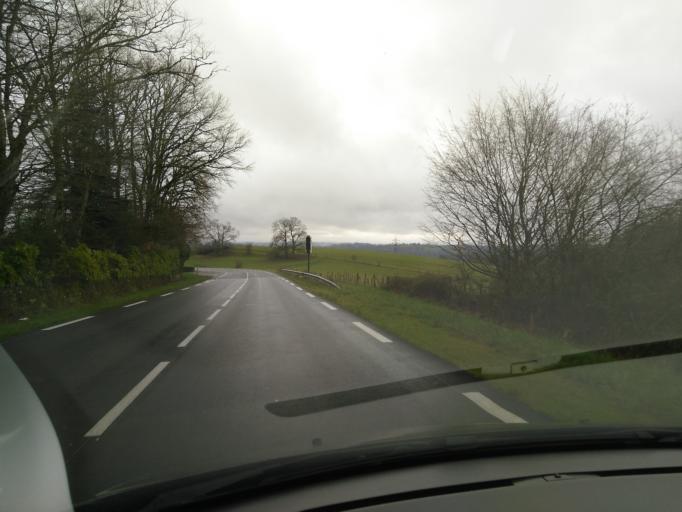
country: FR
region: Limousin
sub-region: Departement de la Haute-Vienne
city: Le Vigen
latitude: 45.7681
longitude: 1.2910
